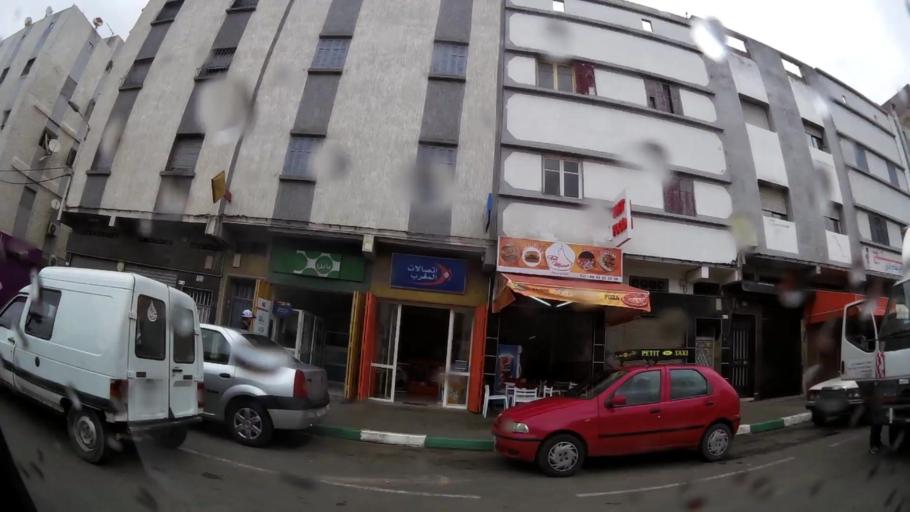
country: MA
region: Grand Casablanca
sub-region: Mediouna
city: Tit Mellil
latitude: 33.6070
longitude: -7.5105
